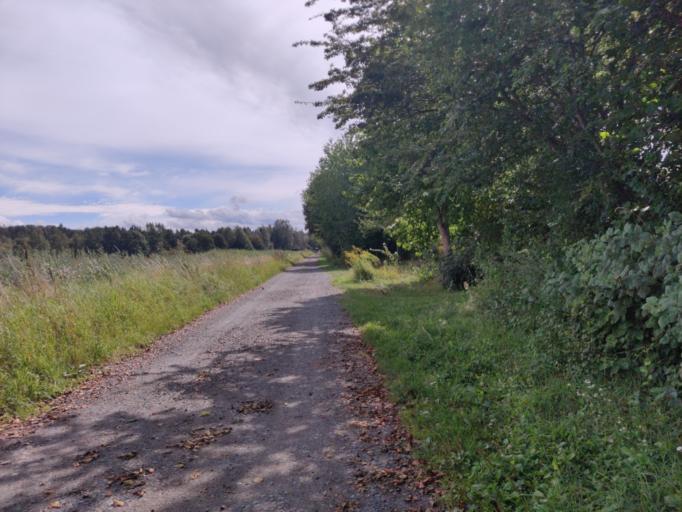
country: DE
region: Lower Saxony
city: Langelsheim
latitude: 51.9794
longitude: 10.3680
